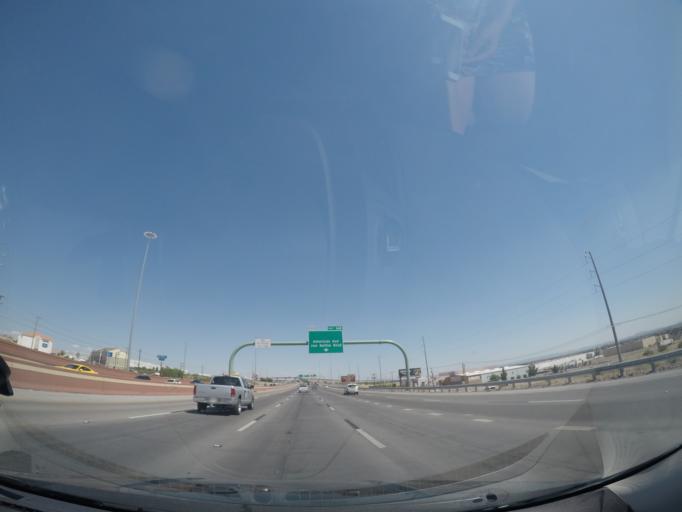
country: US
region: Texas
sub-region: El Paso County
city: Socorro
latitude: 31.7117
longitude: -106.2958
